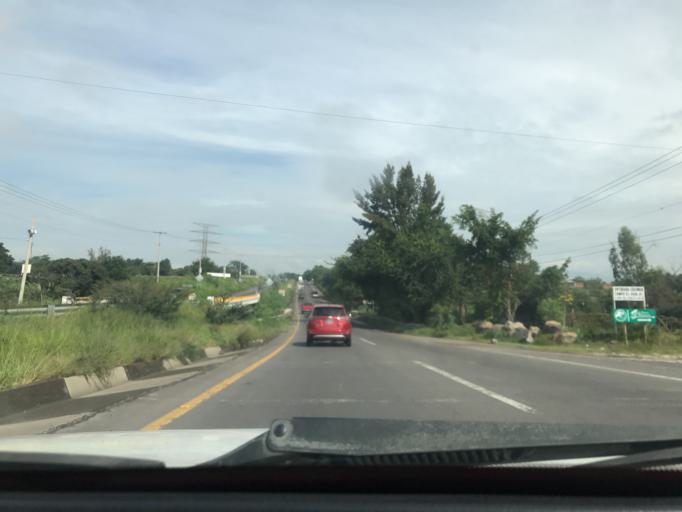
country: MX
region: Morelos
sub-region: Yecapixtla
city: Juan Morales
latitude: 18.8398
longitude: -98.9248
